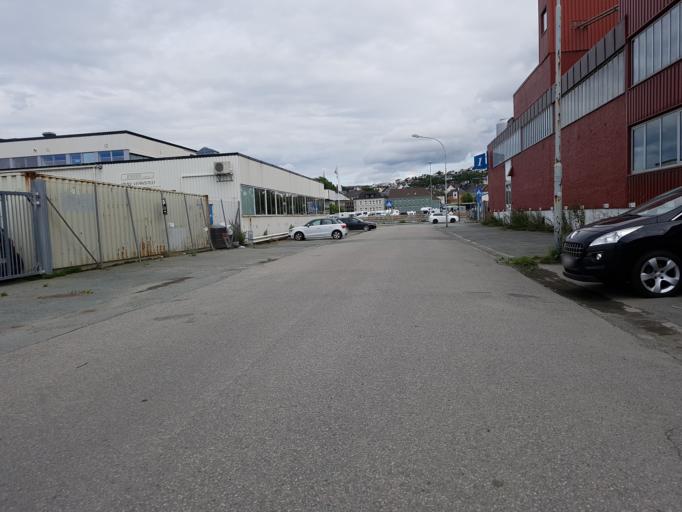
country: NO
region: Sor-Trondelag
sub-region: Trondheim
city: Trondheim
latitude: 63.4386
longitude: 10.4162
